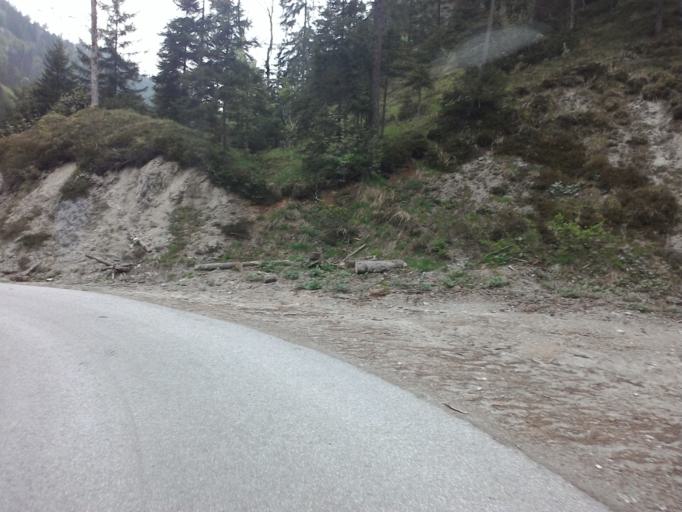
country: AT
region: Styria
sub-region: Politischer Bezirk Liezen
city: Wildalpen
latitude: 47.7039
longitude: 15.0066
